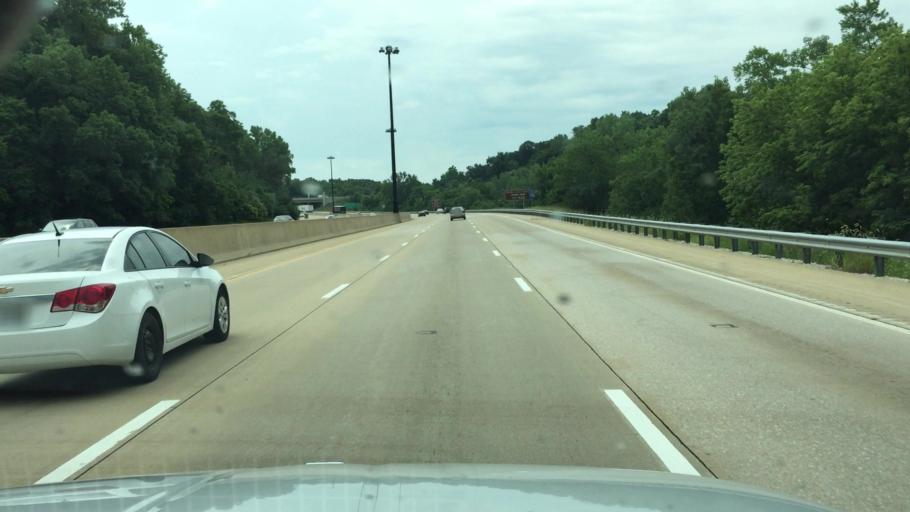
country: US
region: Illinois
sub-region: Peoria County
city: West Peoria
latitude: 40.7150
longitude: -89.6217
